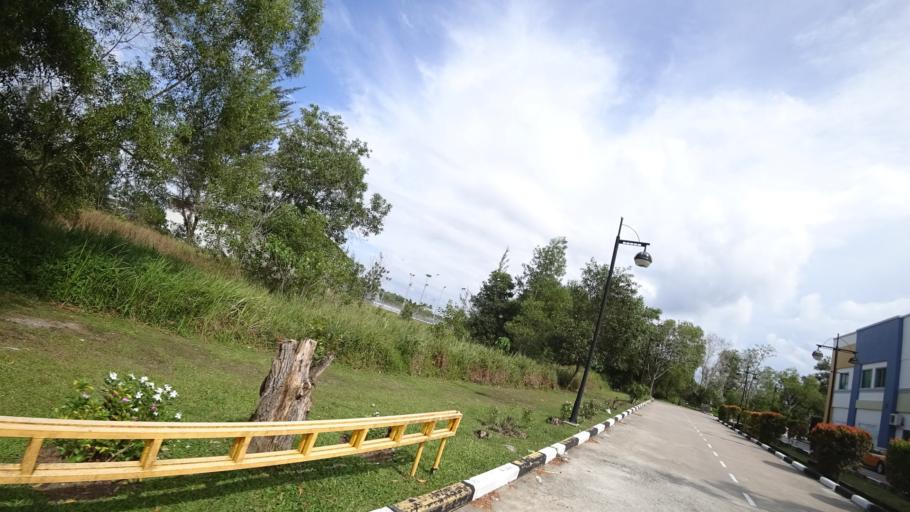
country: BN
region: Tutong
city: Tutong
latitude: 4.8130
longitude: 114.6571
